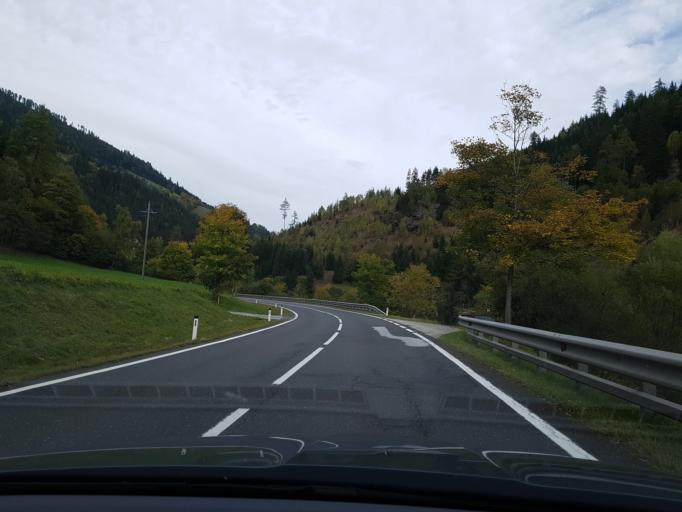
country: AT
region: Salzburg
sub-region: Politischer Bezirk Tamsweg
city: Ramingstein
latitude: 47.0797
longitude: 13.8128
